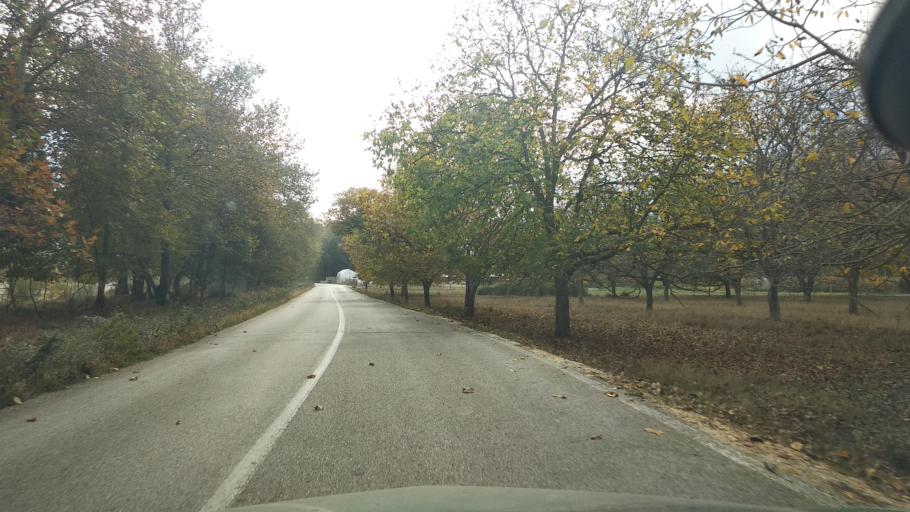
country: GR
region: Thessaly
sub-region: Trikala
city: Kastraki
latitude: 39.7138
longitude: 21.5257
